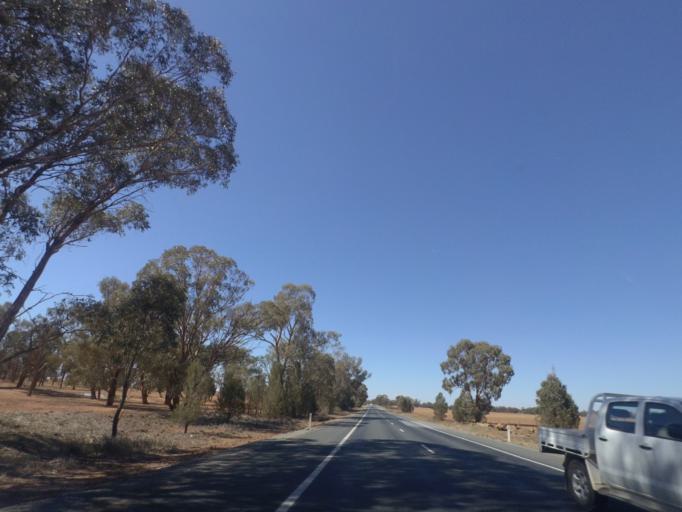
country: AU
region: New South Wales
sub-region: Bland
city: West Wyalong
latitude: -34.1865
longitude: 147.1124
